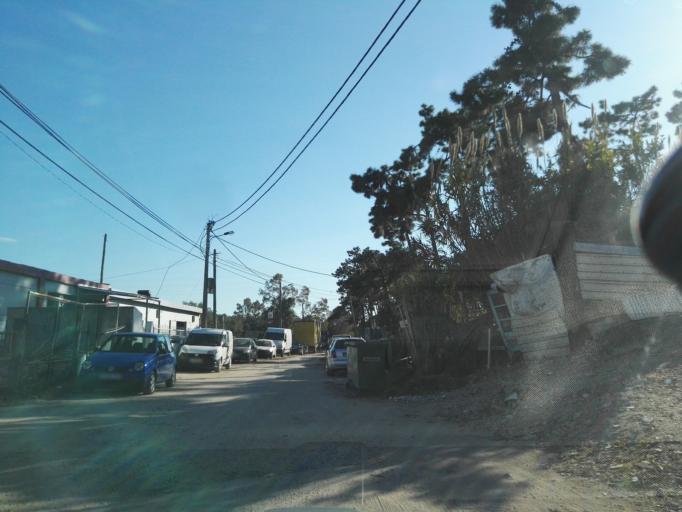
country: PT
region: Setubal
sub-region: Seixal
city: Corroios
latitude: 38.6275
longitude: -9.1456
